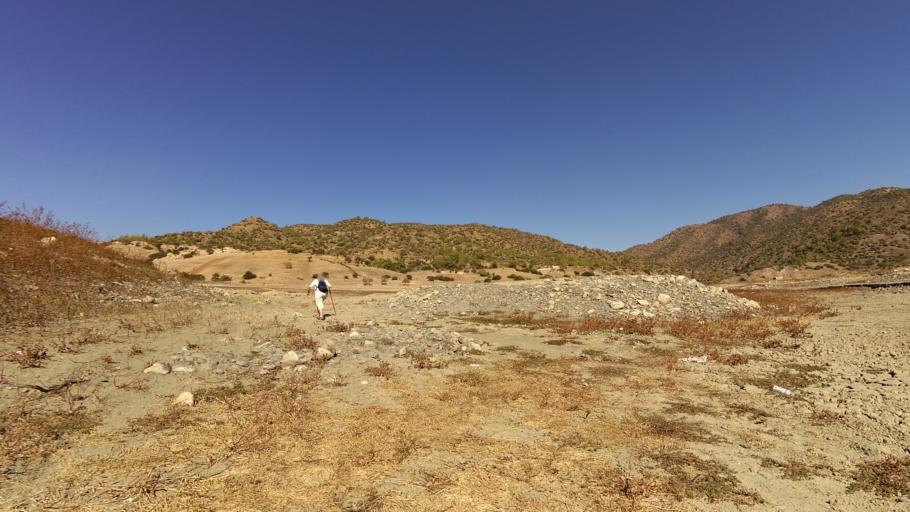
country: CY
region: Limassol
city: Mouttagiaka
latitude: 34.7578
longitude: 33.0915
